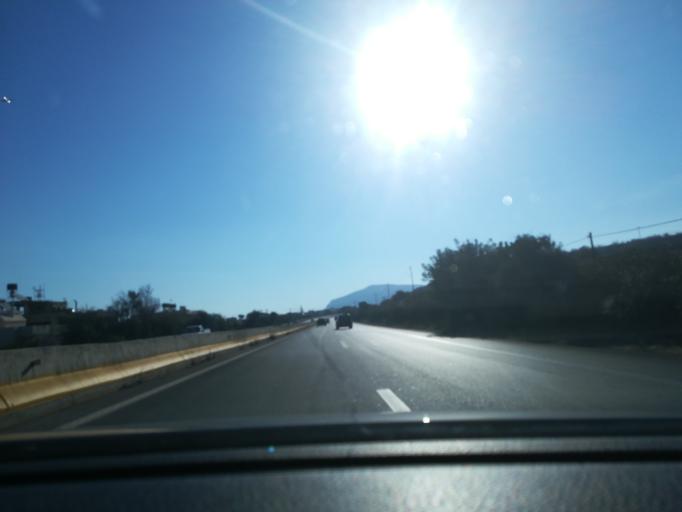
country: GR
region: Crete
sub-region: Nomos Irakleiou
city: Kokkini Hani
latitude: 35.3289
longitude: 25.2670
